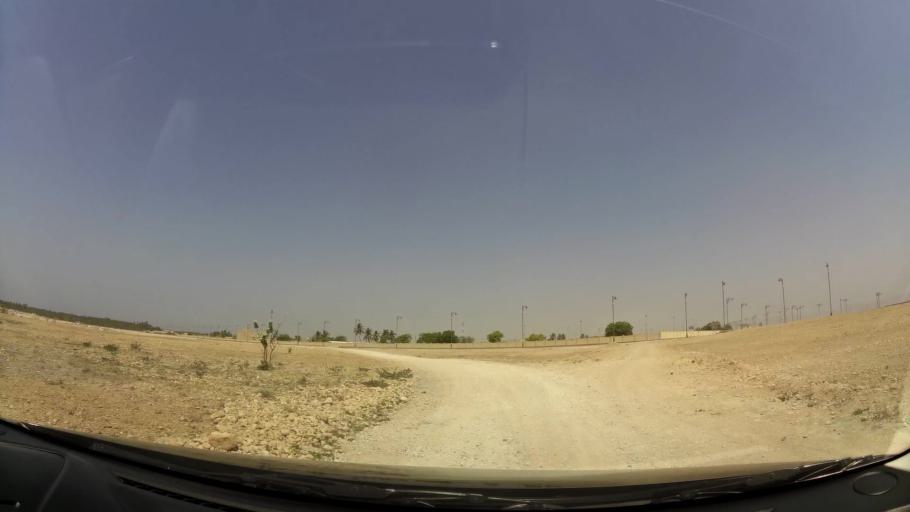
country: OM
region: Zufar
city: Salalah
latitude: 17.0485
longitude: 54.2247
